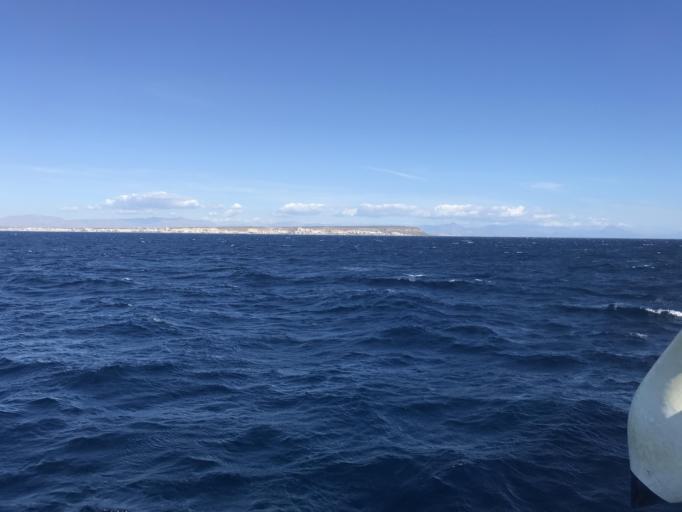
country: ES
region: Valencia
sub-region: Provincia de Alicante
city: Santa Pola
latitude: 38.1346
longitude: -0.5316
